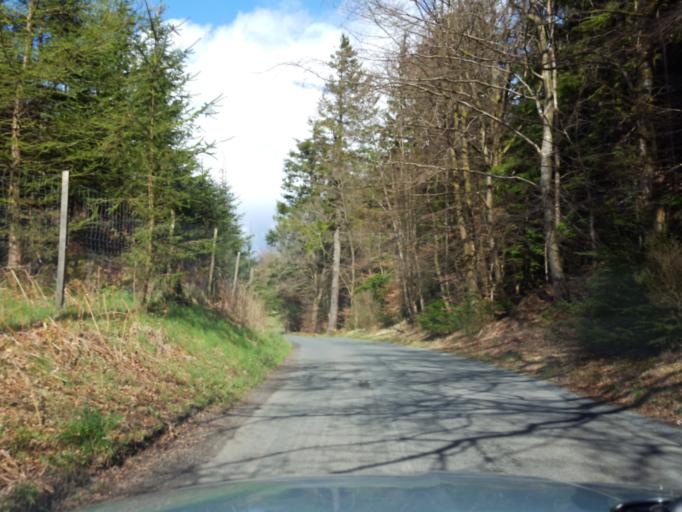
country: GB
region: Scotland
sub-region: Clackmannanshire
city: Dollar
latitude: 56.2020
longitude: -3.6034
